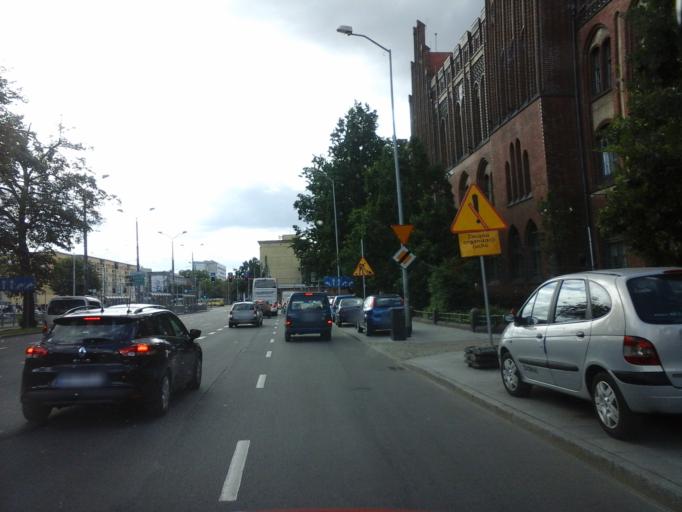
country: PL
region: West Pomeranian Voivodeship
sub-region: Szczecin
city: Szczecin
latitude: 53.4267
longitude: 14.5513
